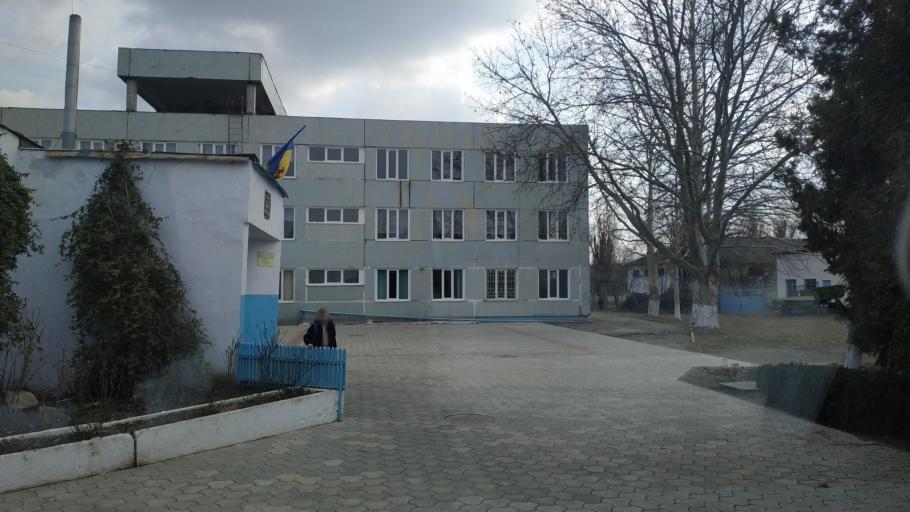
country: MD
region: Anenii Noi
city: Anenii Noi
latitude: 46.9009
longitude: 29.1386
